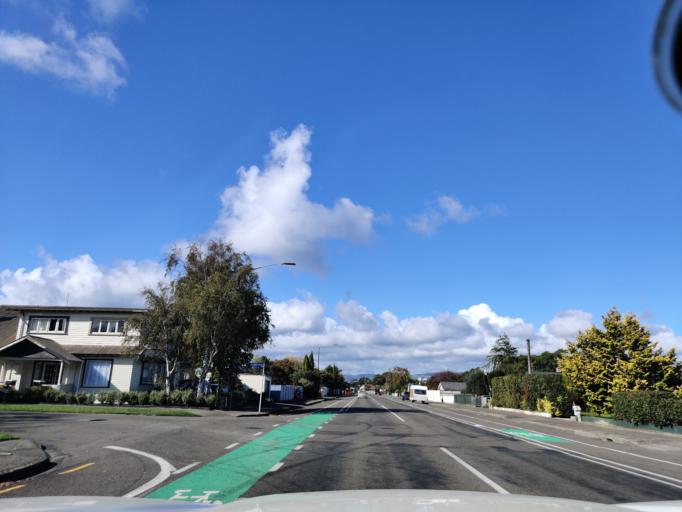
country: NZ
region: Manawatu-Wanganui
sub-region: Palmerston North City
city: Palmerston North
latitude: -40.3507
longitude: 175.5979
